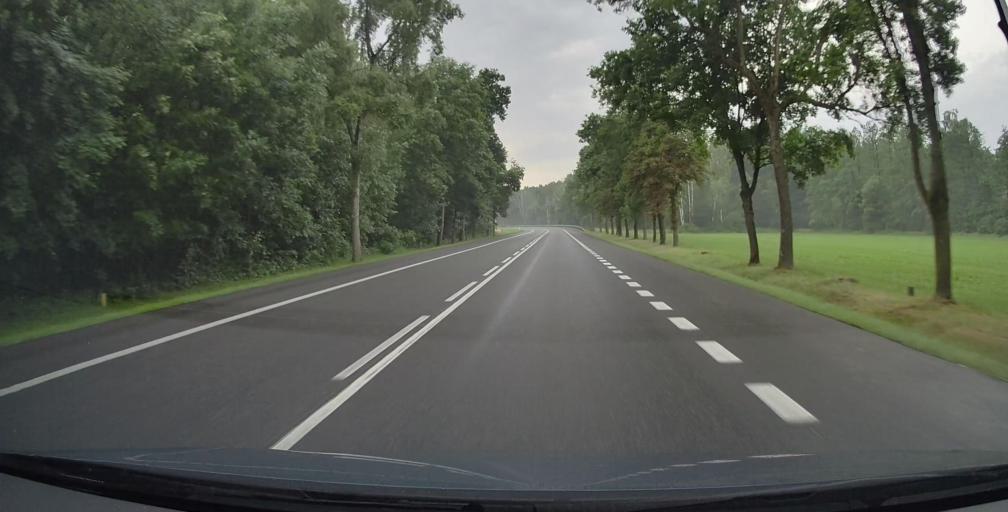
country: PL
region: Masovian Voivodeship
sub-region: Powiat siedlecki
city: Zbuczyn
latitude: 52.0803
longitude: 22.4830
